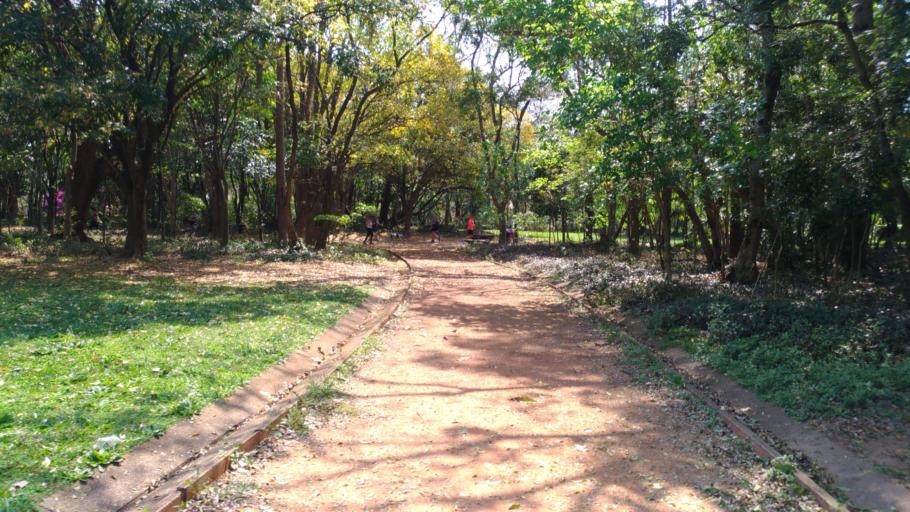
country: BR
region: Sao Paulo
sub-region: Osasco
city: Osasco
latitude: -23.5457
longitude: -46.7208
